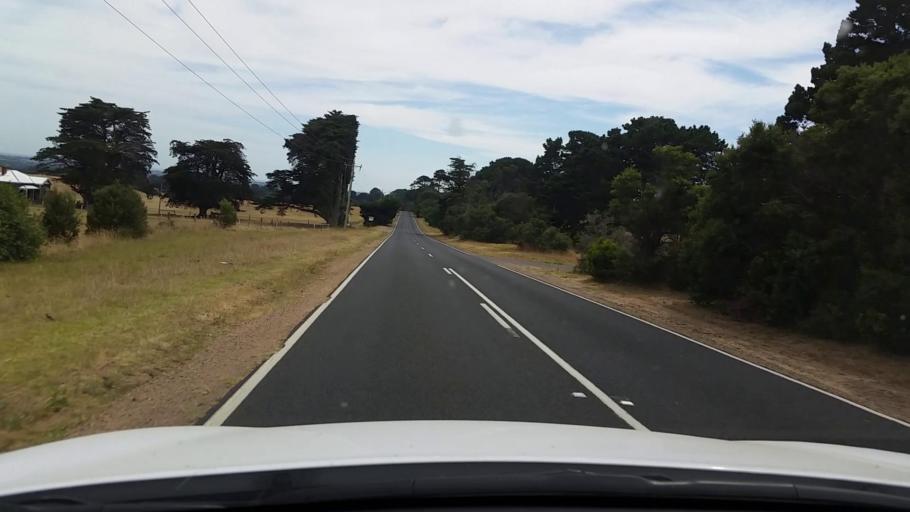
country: AU
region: Victoria
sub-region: Mornington Peninsula
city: Saint Andrews Beach
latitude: -38.4427
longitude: 144.8967
